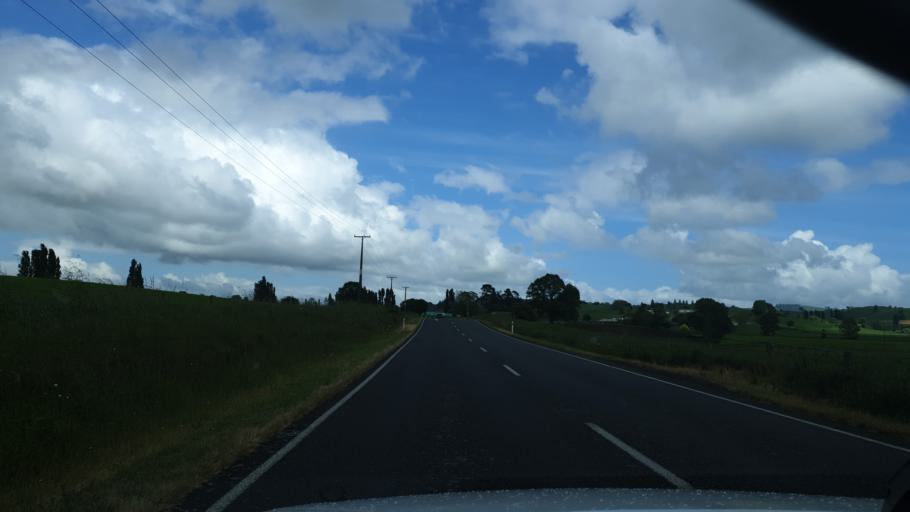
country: NZ
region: Waikato
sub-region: Matamata-Piako District
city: Matamata
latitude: -37.8772
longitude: 175.7176
